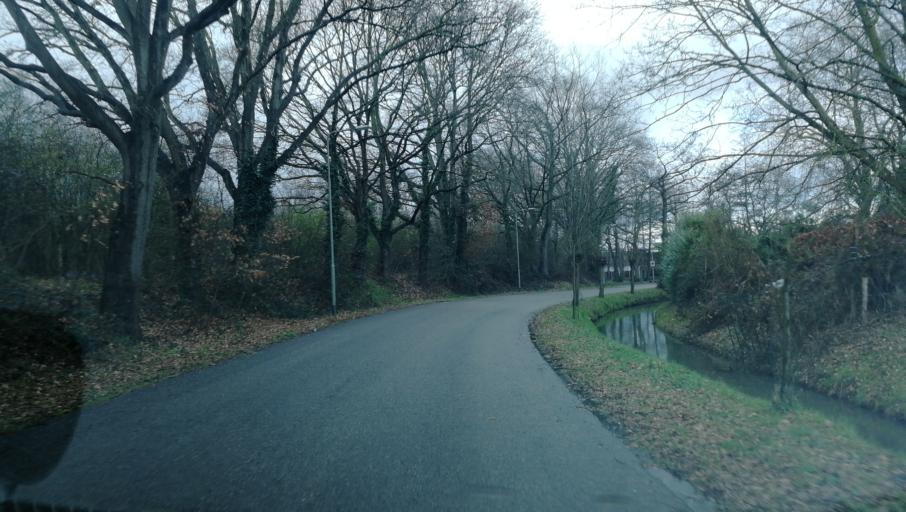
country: NL
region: Limburg
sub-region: Gemeente Venlo
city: Tegelen
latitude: 51.3300
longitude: 6.1348
